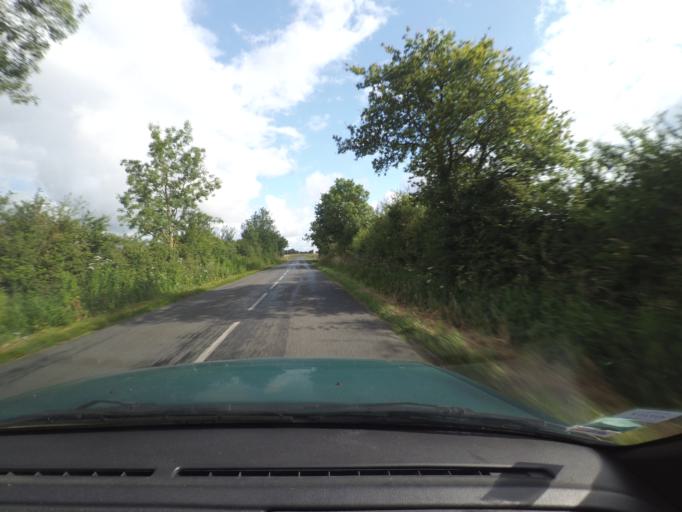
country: FR
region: Pays de la Loire
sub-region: Departement de la Loire-Atlantique
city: Saint-Hilaire-de-Clisson
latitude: 47.0385
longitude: -1.3245
